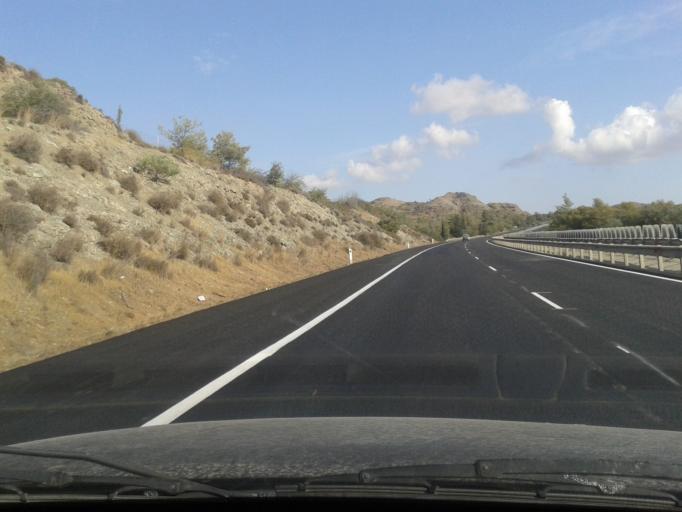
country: CY
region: Larnaka
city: Kornos
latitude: 34.8810
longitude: 33.3964
